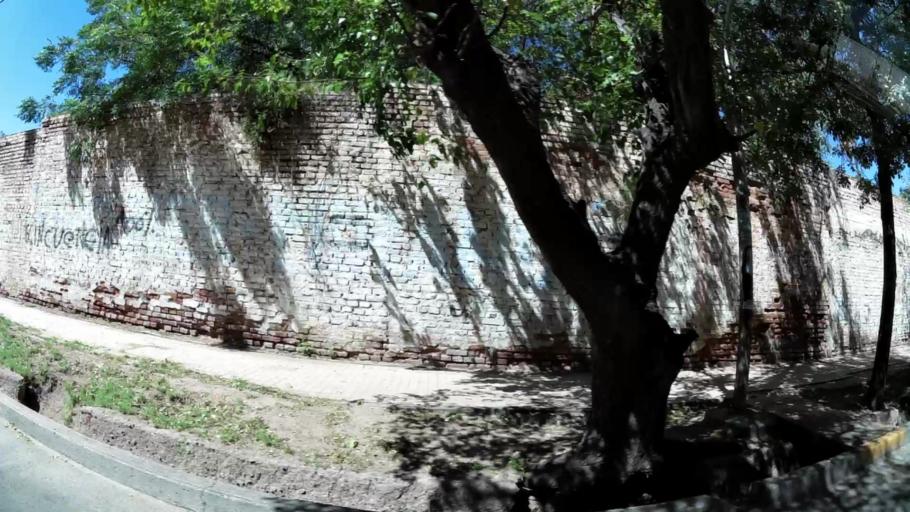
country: AR
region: Mendoza
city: Las Heras
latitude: -32.8563
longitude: -68.8375
